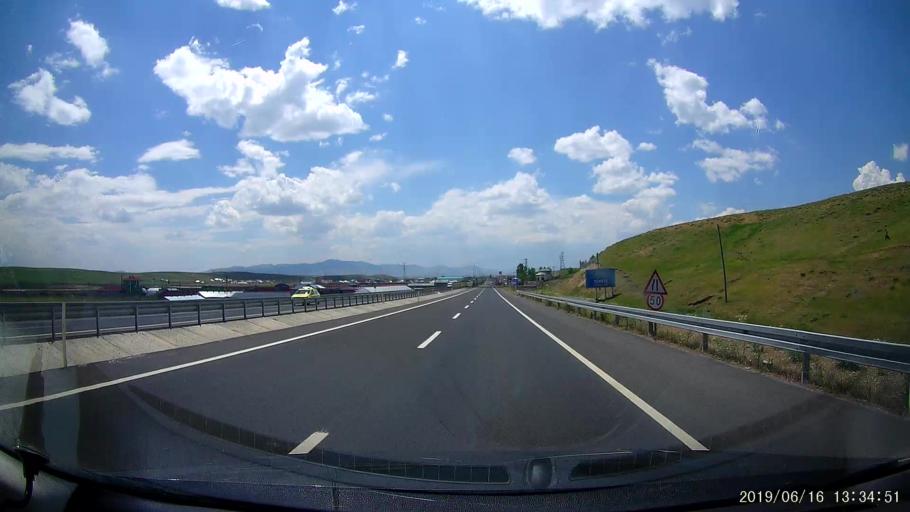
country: TR
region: Agri
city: Agri
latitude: 39.7129
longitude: 43.1162
